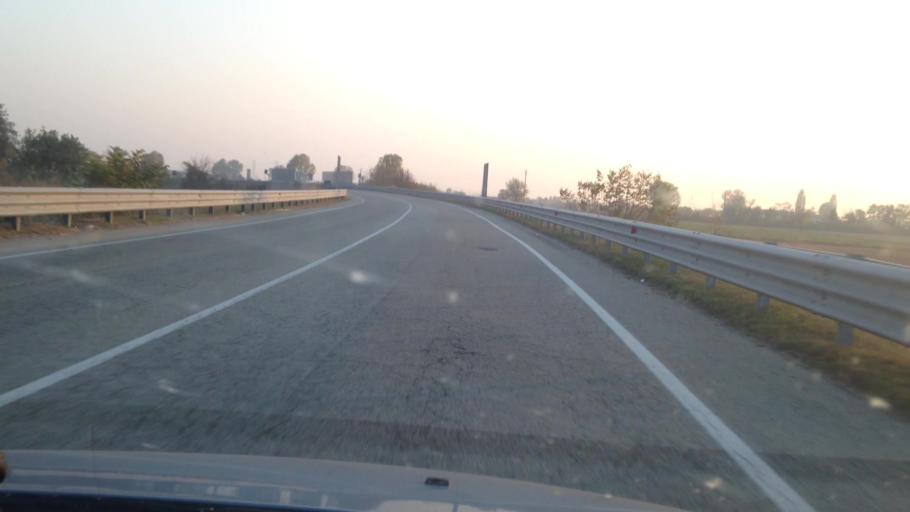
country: IT
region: Piedmont
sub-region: Provincia di Vercelli
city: Cigliano
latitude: 45.3078
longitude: 8.0408
